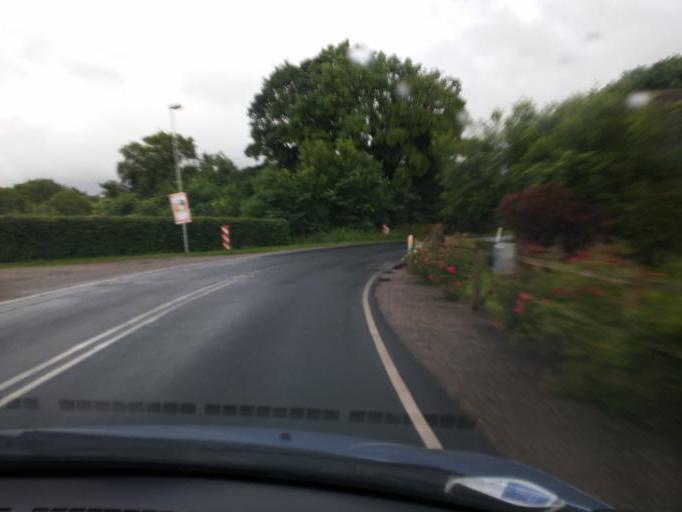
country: DK
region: South Denmark
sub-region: Kerteminde Kommune
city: Kerteminde
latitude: 55.5034
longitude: 10.6500
